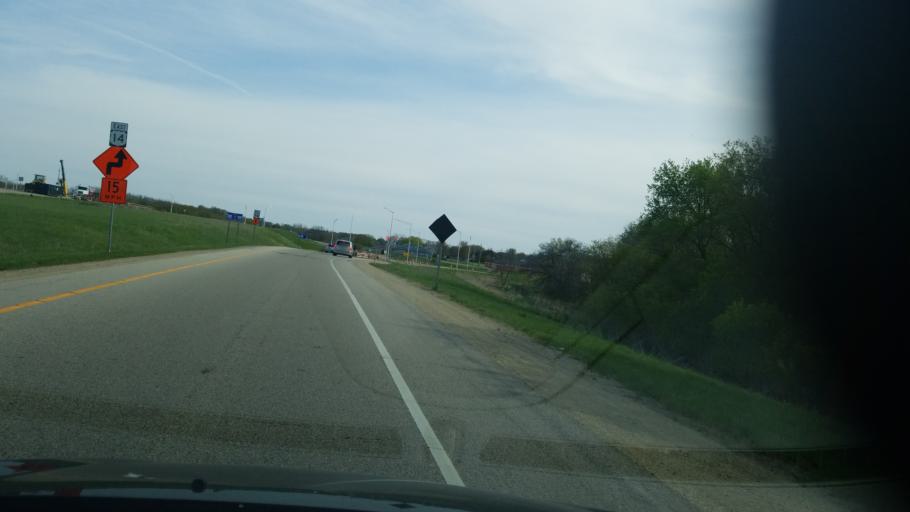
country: US
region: Wisconsin
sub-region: Dane County
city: Oregon
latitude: 42.9198
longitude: -89.3681
